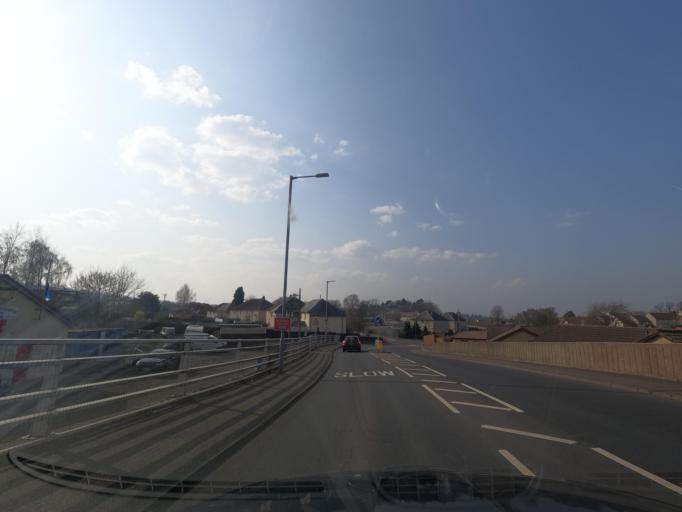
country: GB
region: Scotland
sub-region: Falkirk
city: Polmont
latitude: 55.9858
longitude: -3.7355
